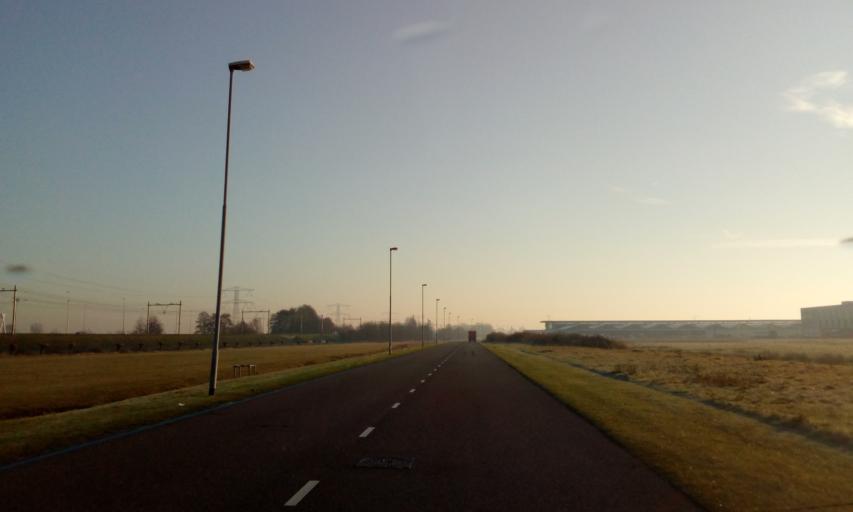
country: NL
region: South Holland
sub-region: Gemeente Lansingerland
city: Bleiswijk
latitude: 52.0325
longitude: 4.5487
